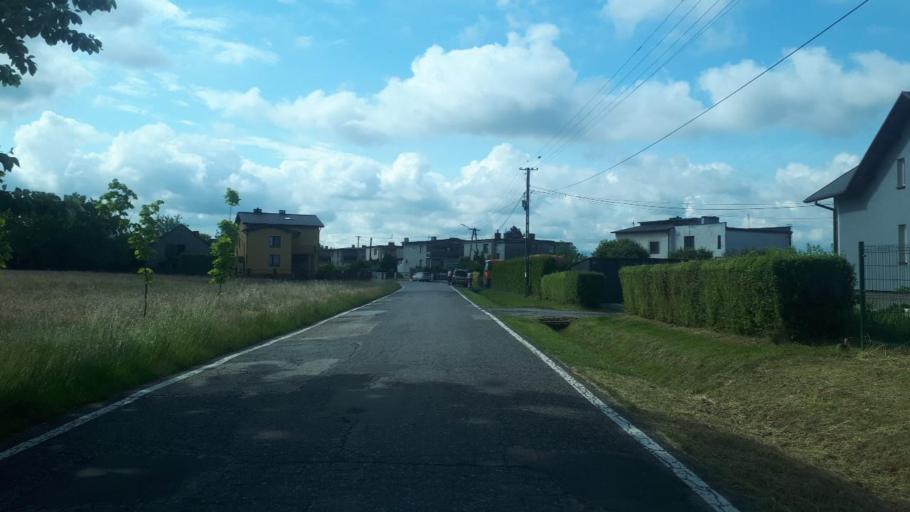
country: PL
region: Silesian Voivodeship
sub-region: Powiat pszczynski
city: Miedzna
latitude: 49.9692
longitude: 19.0206
